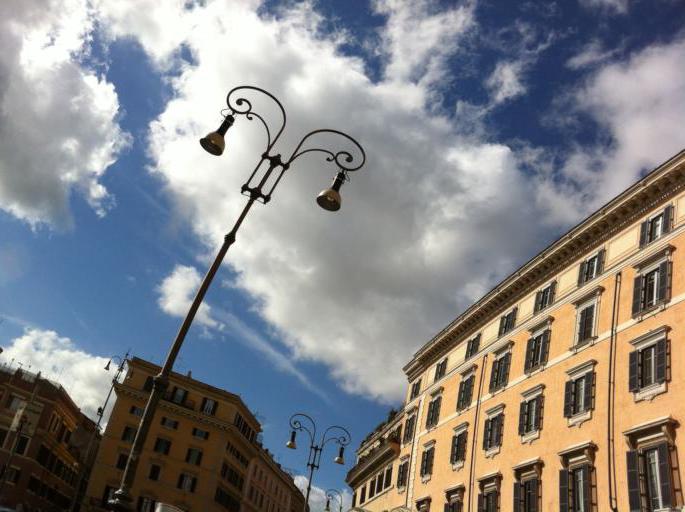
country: VA
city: Vatican City
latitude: 41.8961
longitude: 12.4774
